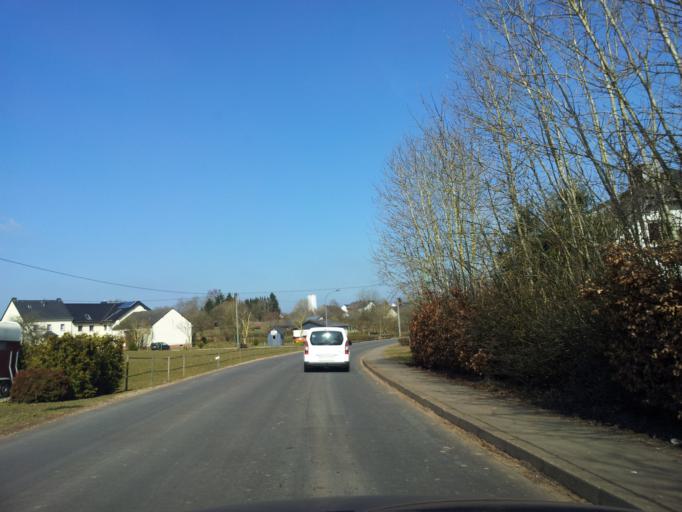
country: DE
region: Rheinland-Pfalz
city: Grosslangenfeld
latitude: 50.2172
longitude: 6.2523
